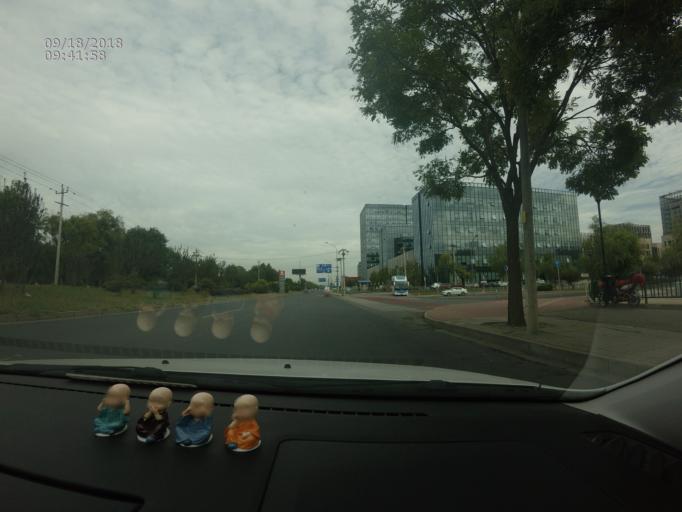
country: CN
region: Beijing
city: Xibeiwang
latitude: 40.0699
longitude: 116.2396
